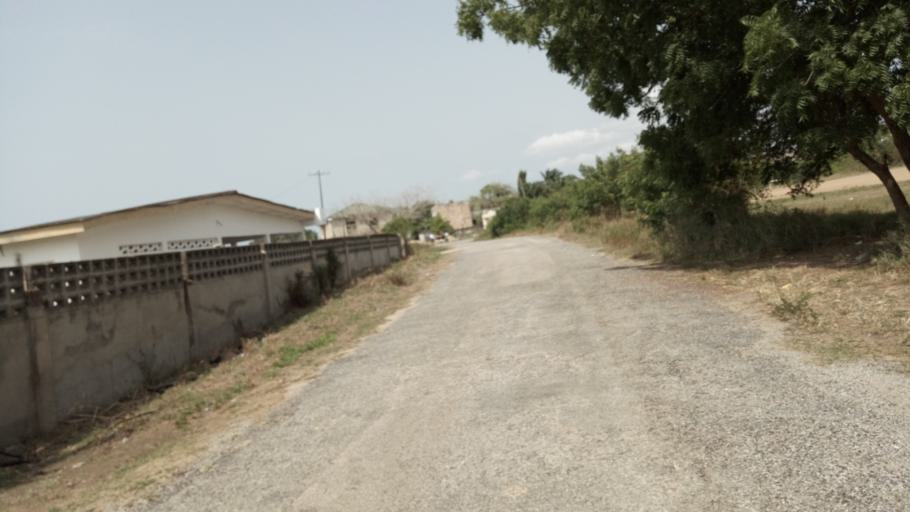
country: GH
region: Central
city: Winneba
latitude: 5.3681
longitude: -0.6419
